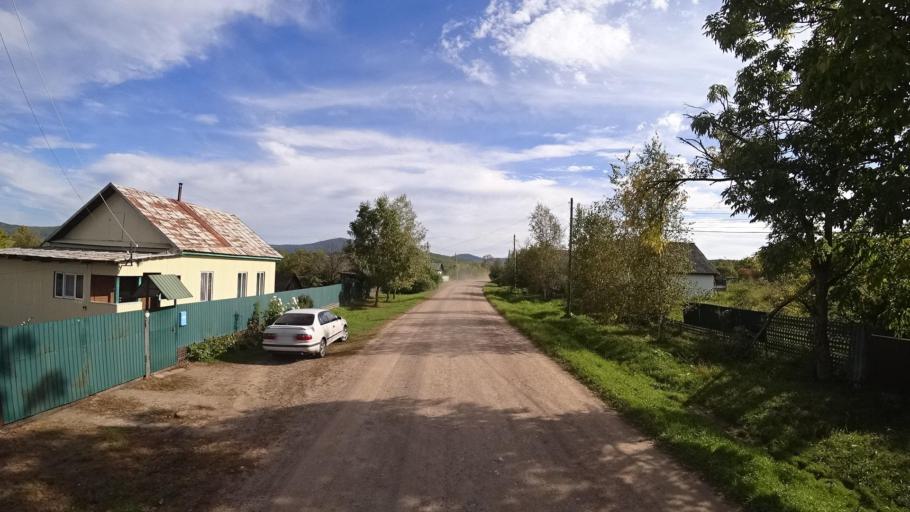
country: RU
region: Primorskiy
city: Dostoyevka
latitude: 44.2997
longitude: 133.4598
